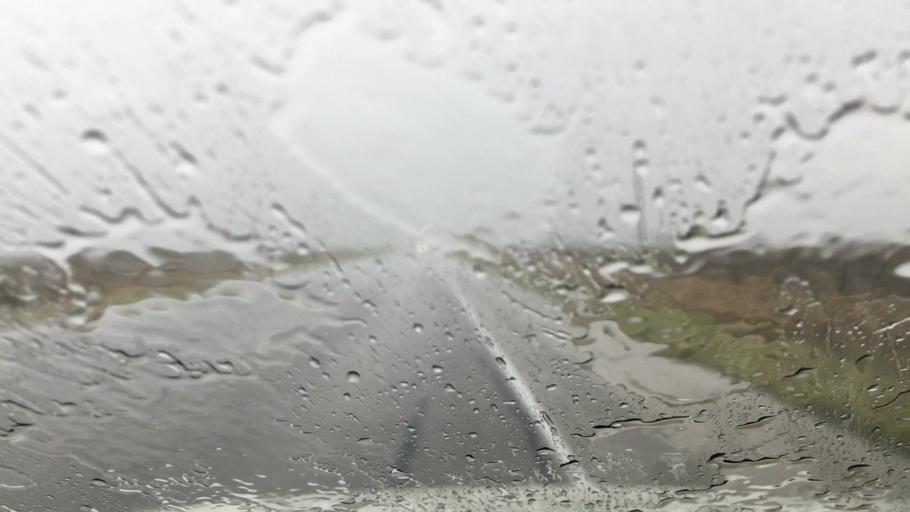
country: US
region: New Mexico
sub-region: Lea County
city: Lovington
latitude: 33.2570
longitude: -103.2194
